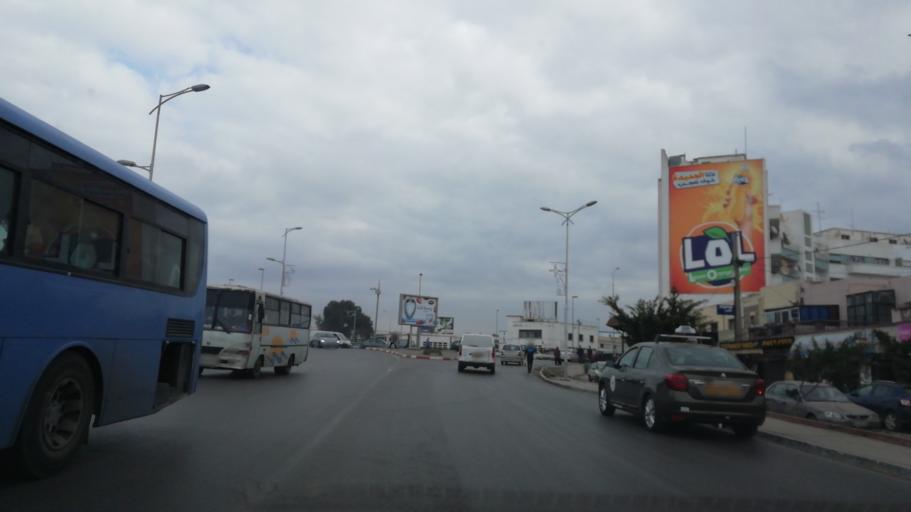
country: DZ
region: Oran
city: Oran
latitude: 35.6963
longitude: -0.6141
